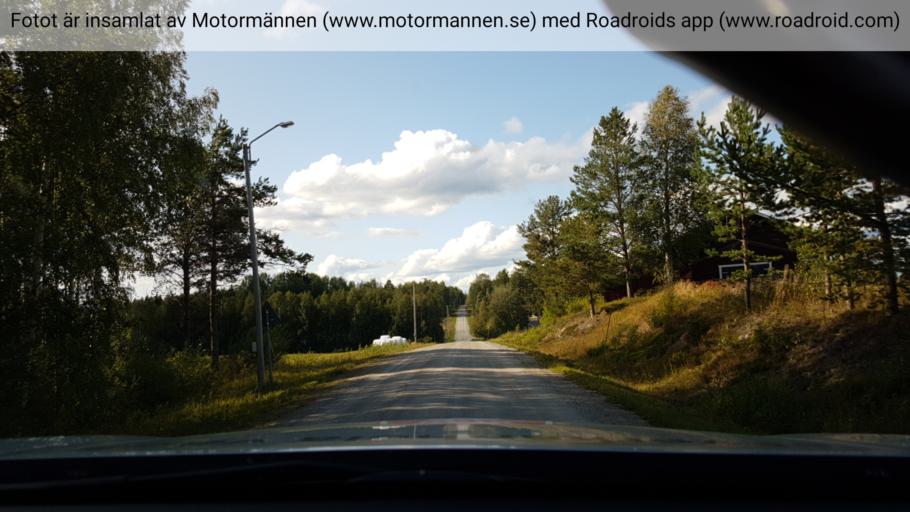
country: SE
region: Vaesterbotten
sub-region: Norsjo Kommun
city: Norsjoe
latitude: 64.6950
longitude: 19.1515
